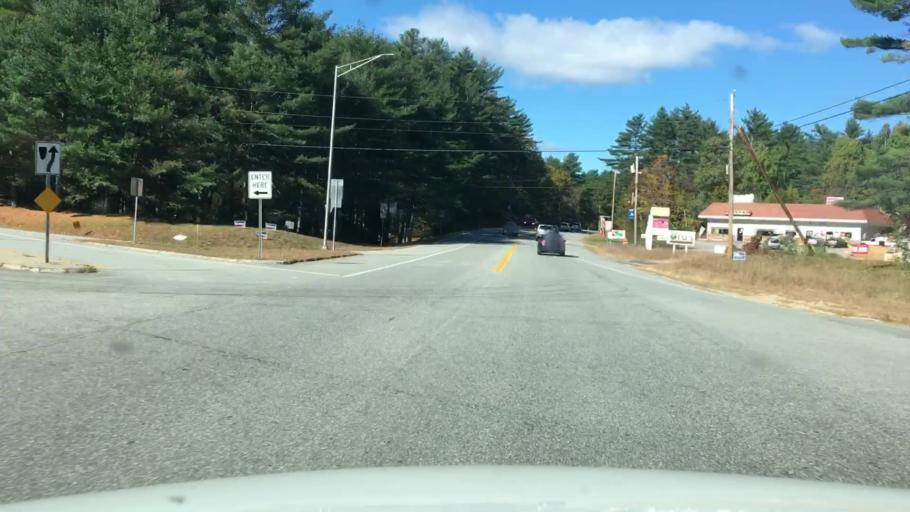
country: US
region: New Hampshire
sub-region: Carroll County
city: Ossipee
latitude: 43.6851
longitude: -71.0886
